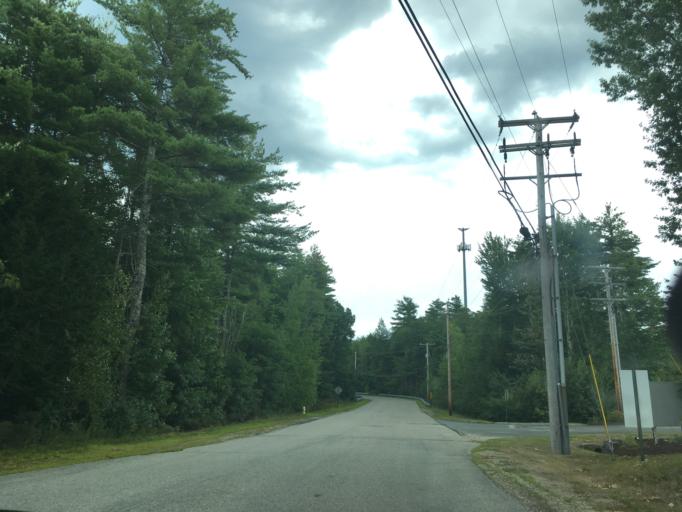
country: US
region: New Hampshire
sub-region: Rockingham County
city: Exeter
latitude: 42.9951
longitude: -70.9790
